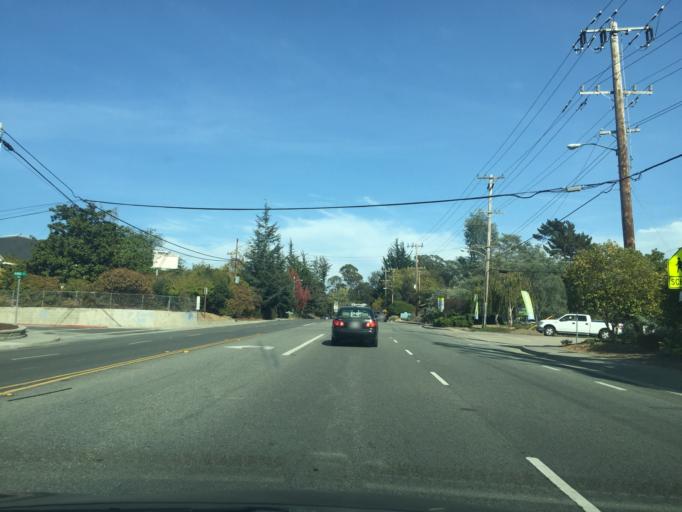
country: US
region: California
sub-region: Santa Cruz County
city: Soquel
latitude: 36.9898
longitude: -121.9334
